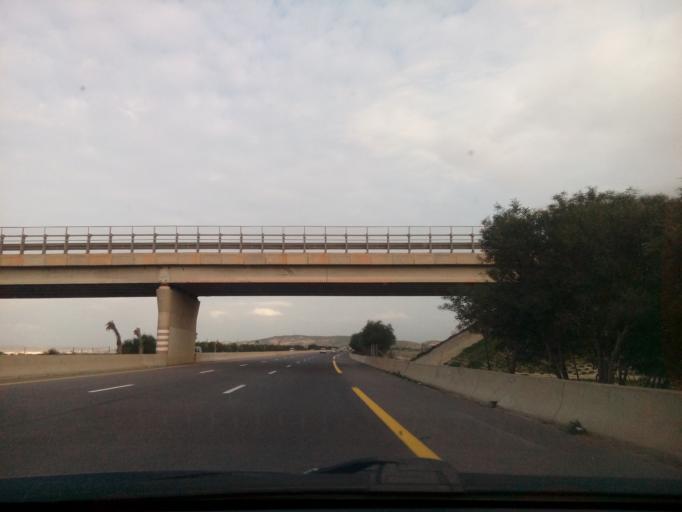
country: DZ
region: Mostaganem
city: Mostaganem
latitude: 35.7039
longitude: 0.1952
